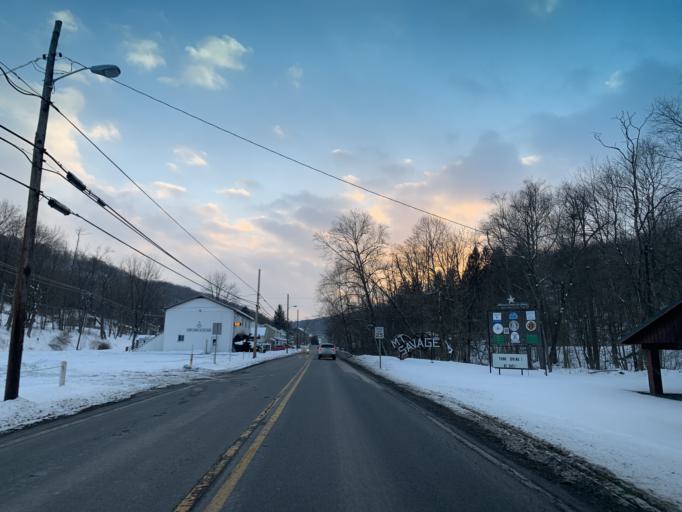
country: US
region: Maryland
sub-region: Allegany County
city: Frostburg
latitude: 39.6986
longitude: -78.8716
